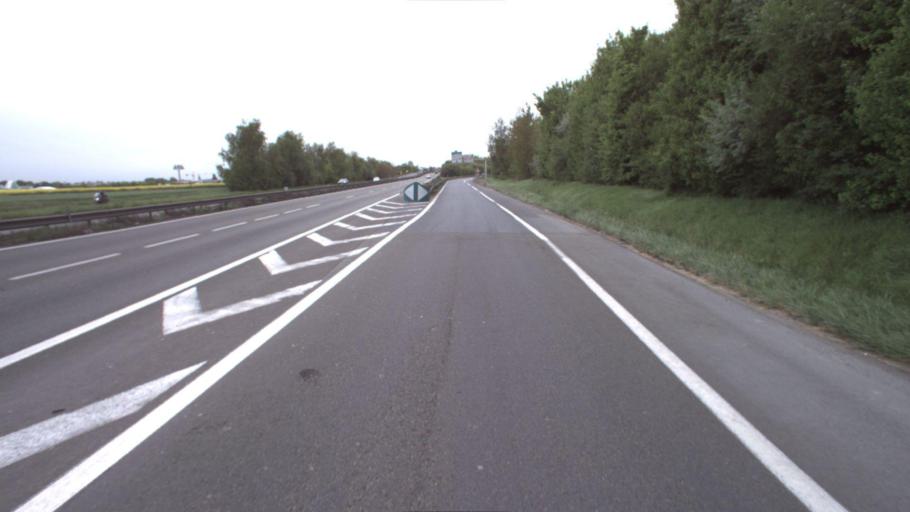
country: FR
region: Ile-de-France
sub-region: Departement de Seine-et-Marne
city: Servon
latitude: 48.7106
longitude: 2.5991
